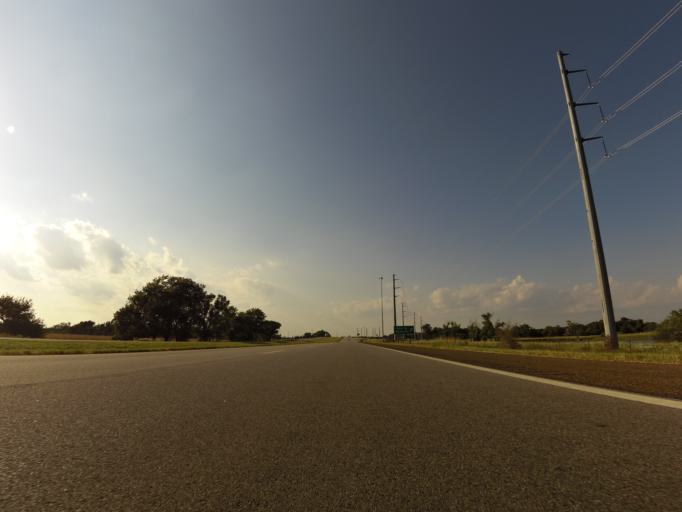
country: US
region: Kansas
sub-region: Sedgwick County
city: Maize
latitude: 37.7761
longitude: -97.4568
